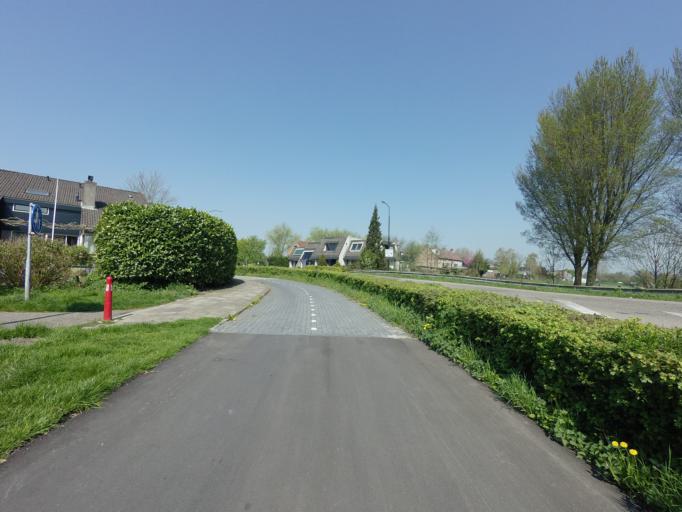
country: NL
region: Utrecht
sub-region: Gemeente De Ronde Venen
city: Mijdrecht
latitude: 52.2123
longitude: 4.8701
